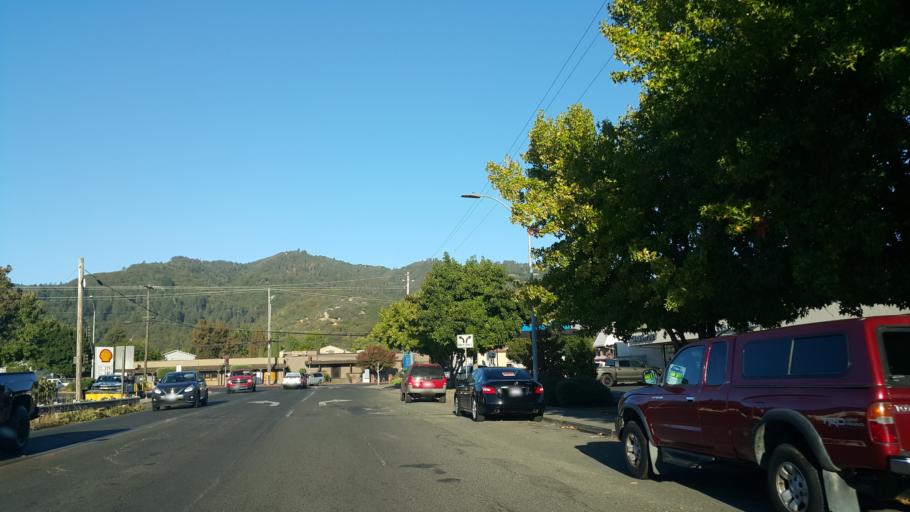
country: US
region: California
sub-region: Mendocino County
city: Ukiah
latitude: 39.1364
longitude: -123.2042
